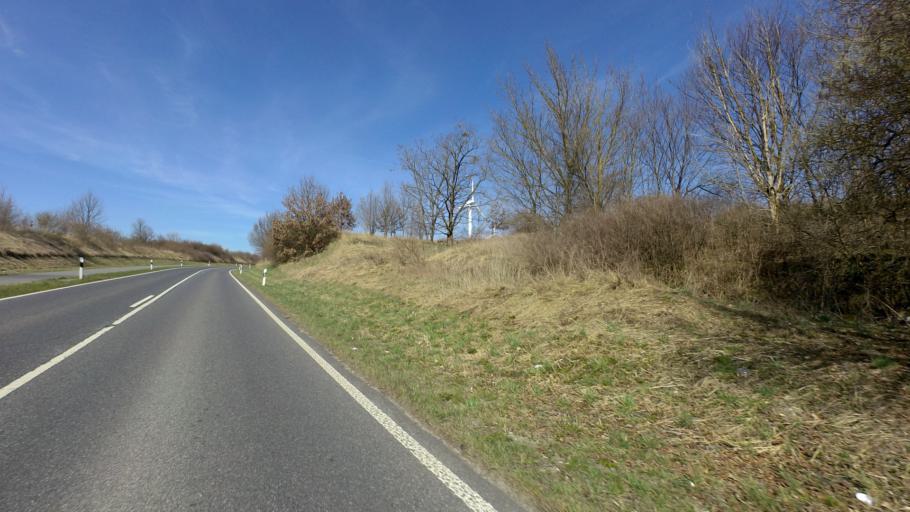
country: DE
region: Brandenburg
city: Furstenwalde
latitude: 52.3841
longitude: 14.0507
